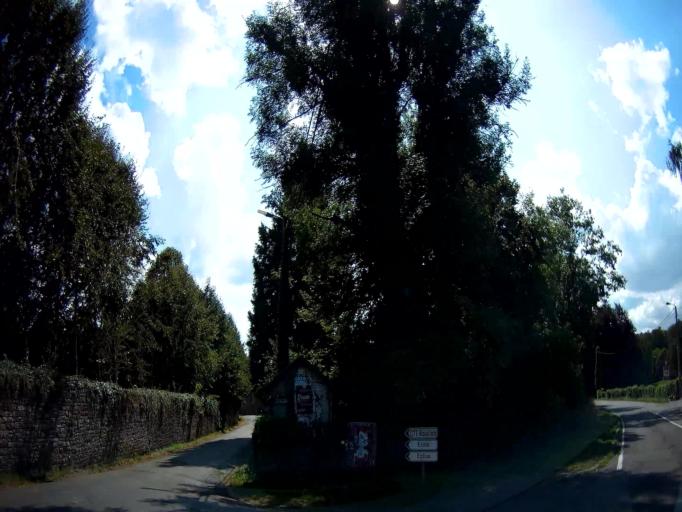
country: BE
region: Wallonia
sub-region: Province de Namur
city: Profondeville
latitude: 50.3444
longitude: 4.8410
